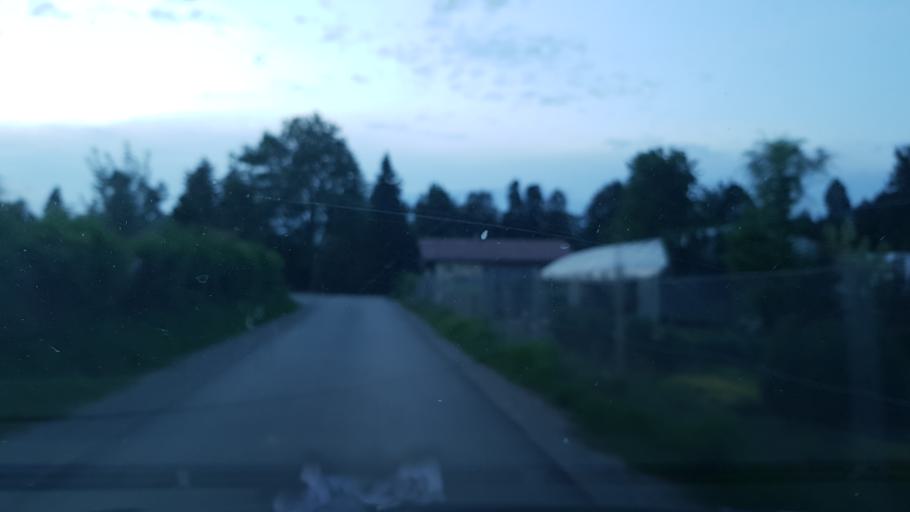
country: SI
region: Postojna
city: Postojna
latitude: 45.7430
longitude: 14.1840
